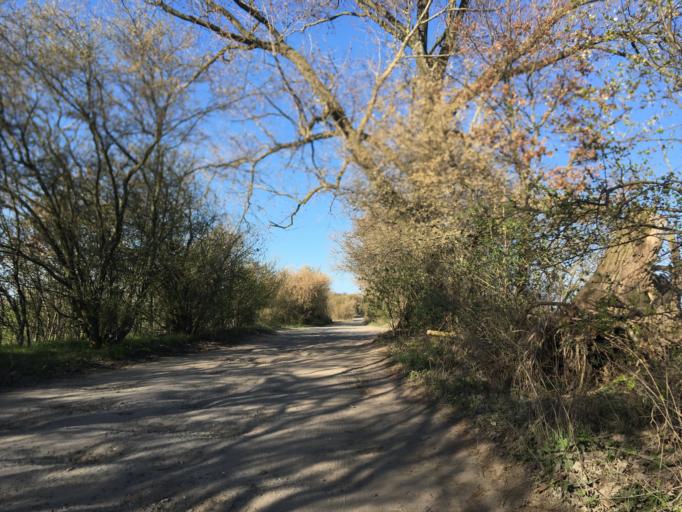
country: DE
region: Brandenburg
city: Ahrensfelde
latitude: 52.6070
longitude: 13.5659
